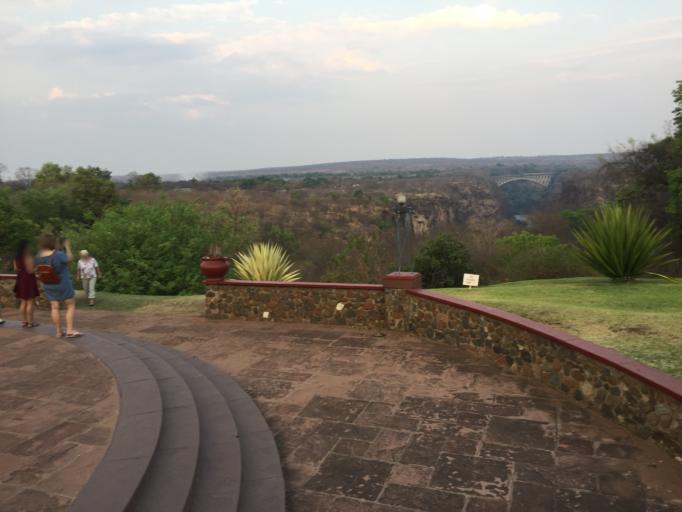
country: ZW
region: Matabeleland North
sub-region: Hwange District
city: Victoria Falls
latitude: -17.9307
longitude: 25.8434
